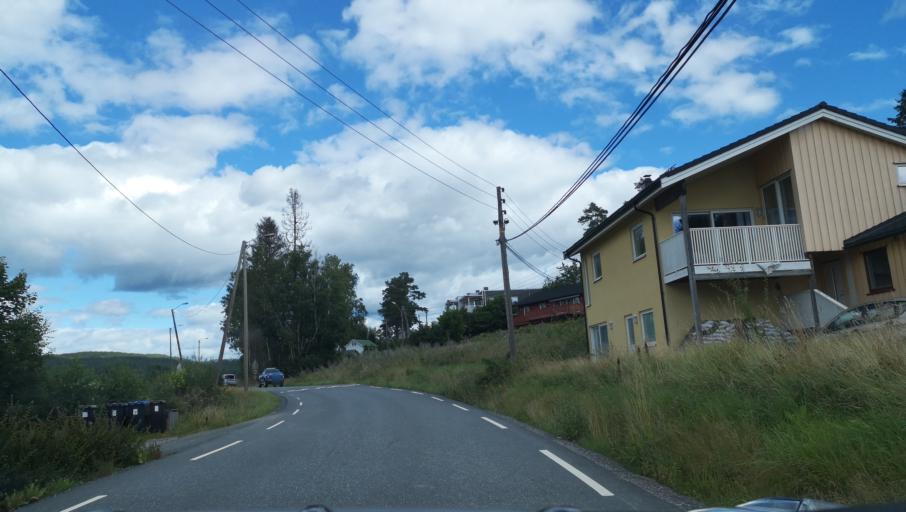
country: NO
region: Ostfold
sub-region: Hobol
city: Tomter
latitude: 59.6658
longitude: 11.0015
